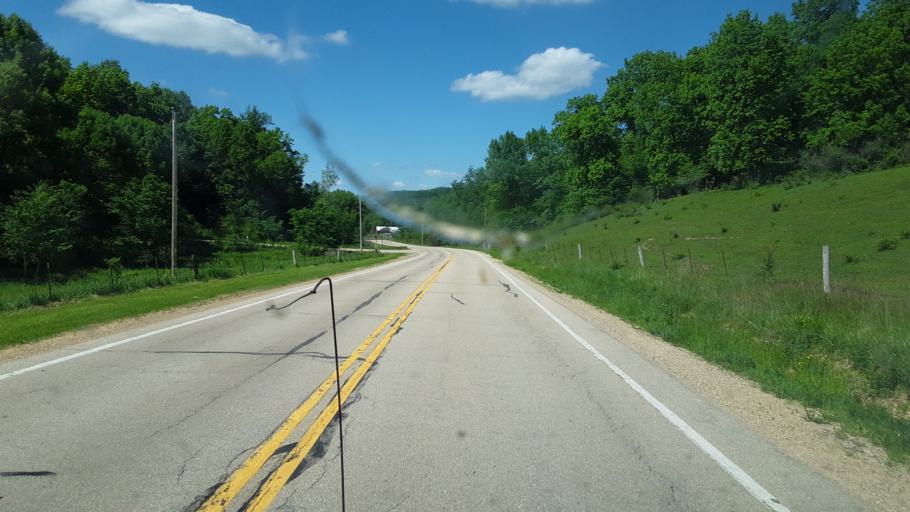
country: US
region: Wisconsin
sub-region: Sauk County
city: Reedsburg
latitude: 43.4833
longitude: -90.2043
